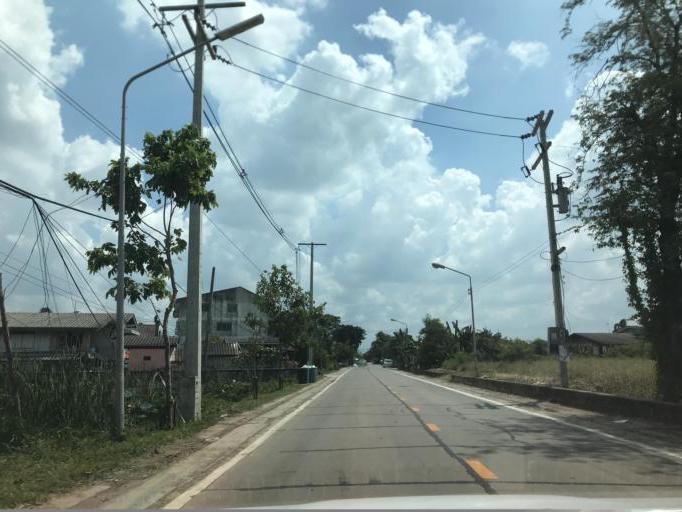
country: TH
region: Pathum Thani
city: Pathum Thani
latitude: 14.0120
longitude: 100.5402
